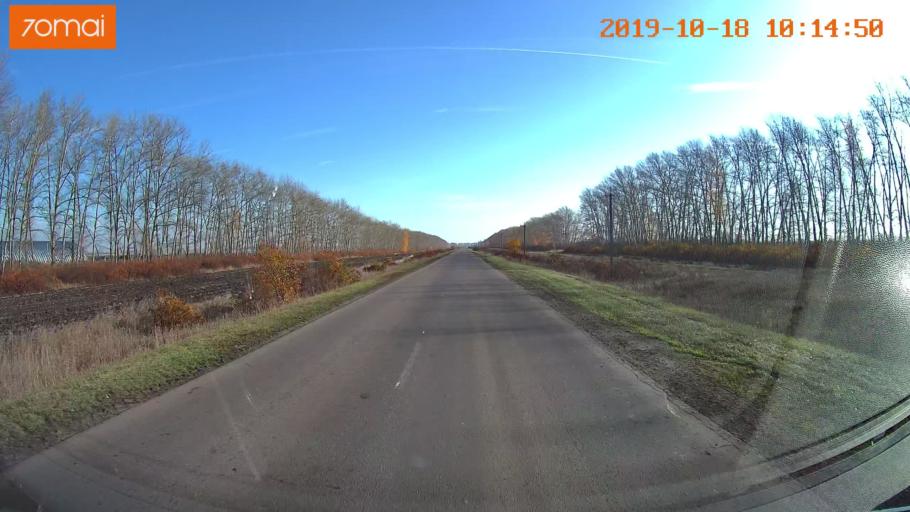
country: RU
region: Tula
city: Kurkino
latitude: 53.4061
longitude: 38.5534
